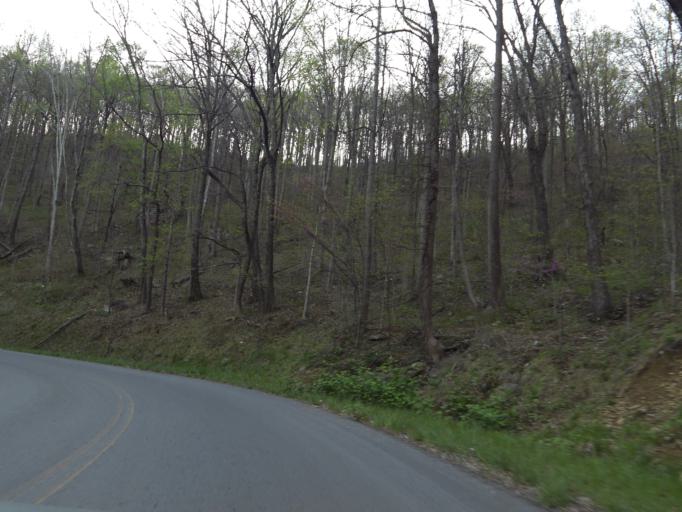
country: US
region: Kentucky
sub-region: Bell County
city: Middlesboro
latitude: 36.6239
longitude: -83.8686
